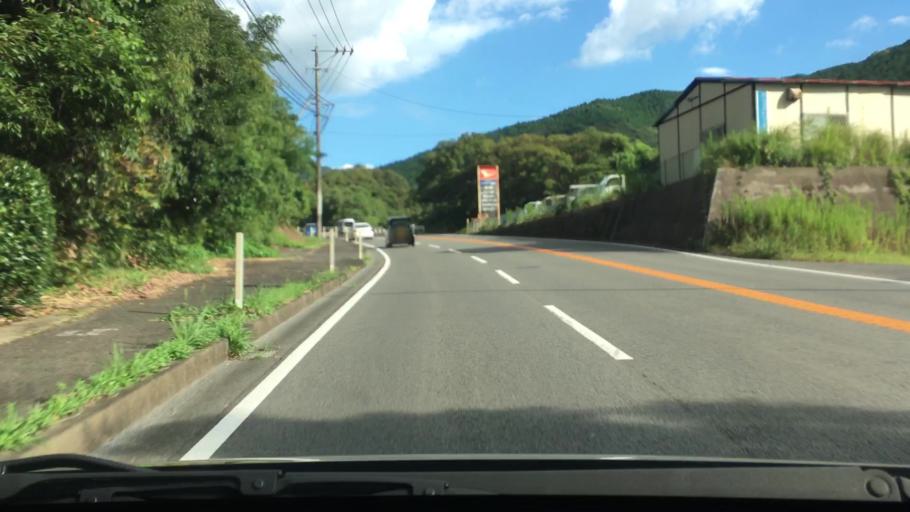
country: JP
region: Nagasaki
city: Togitsu
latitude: 32.8205
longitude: 129.8004
